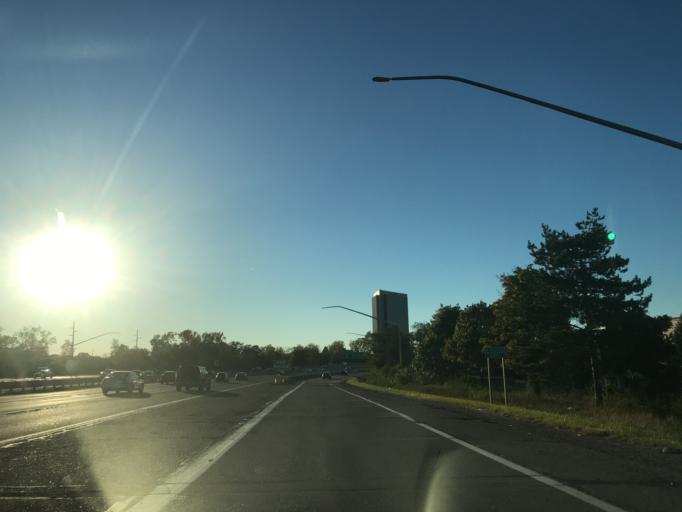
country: US
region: Michigan
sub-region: Oakland County
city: Clawson
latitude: 42.5592
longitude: -83.1500
